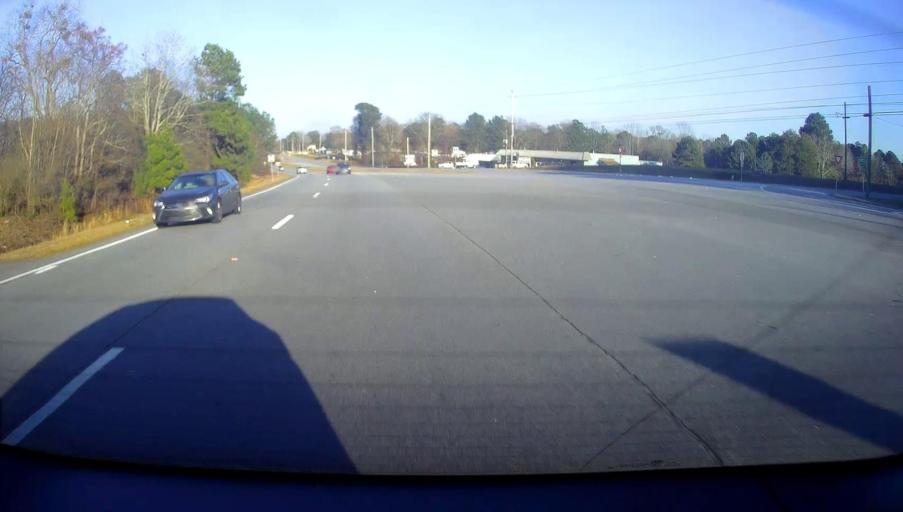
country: US
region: Georgia
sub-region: Fayette County
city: Tyrone
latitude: 33.4431
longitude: -84.5318
